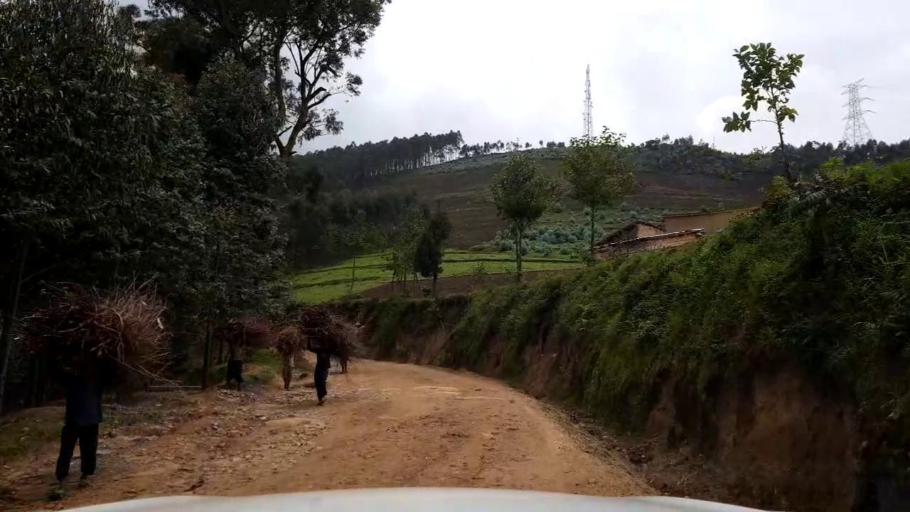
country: RW
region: Western Province
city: Kibuye
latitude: -1.9612
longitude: 29.3939
